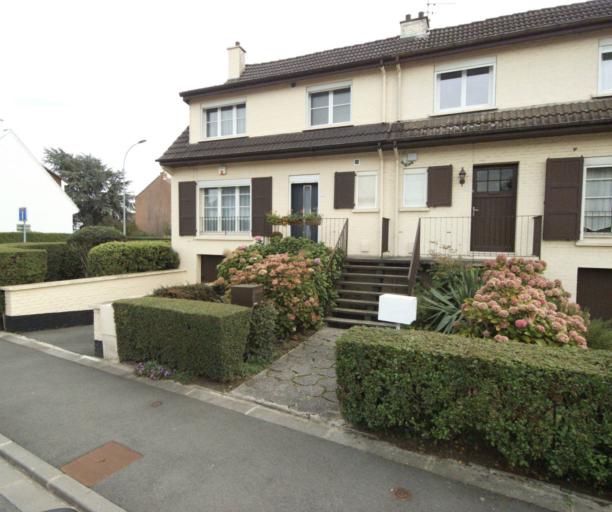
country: FR
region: Nord-Pas-de-Calais
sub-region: Departement du Nord
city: Lambersart
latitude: 50.6517
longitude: 3.0102
